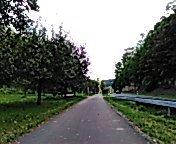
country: LU
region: Grevenmacher
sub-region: Canton d'Echternach
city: Rosport
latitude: 49.7997
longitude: 6.5089
